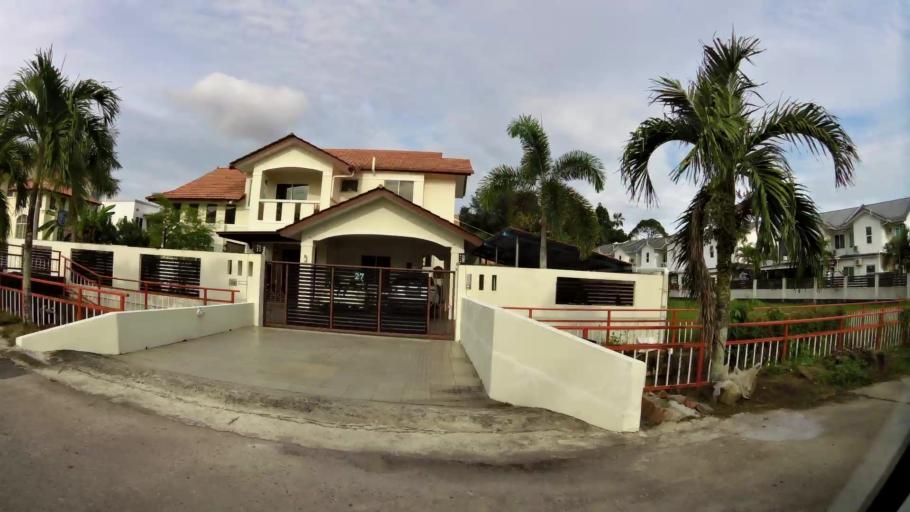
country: BN
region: Brunei and Muara
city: Bandar Seri Begawan
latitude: 4.9013
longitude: 114.8941
